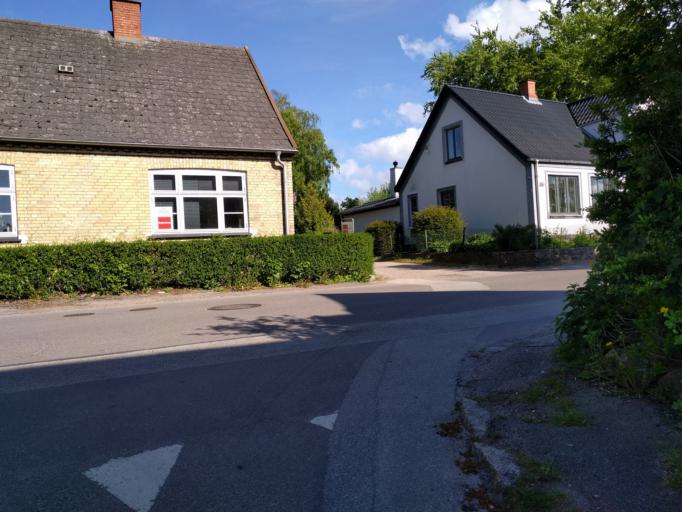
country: DK
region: Zealand
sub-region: Guldborgsund Kommune
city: Stubbekobing
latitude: 54.9253
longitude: 12.0477
